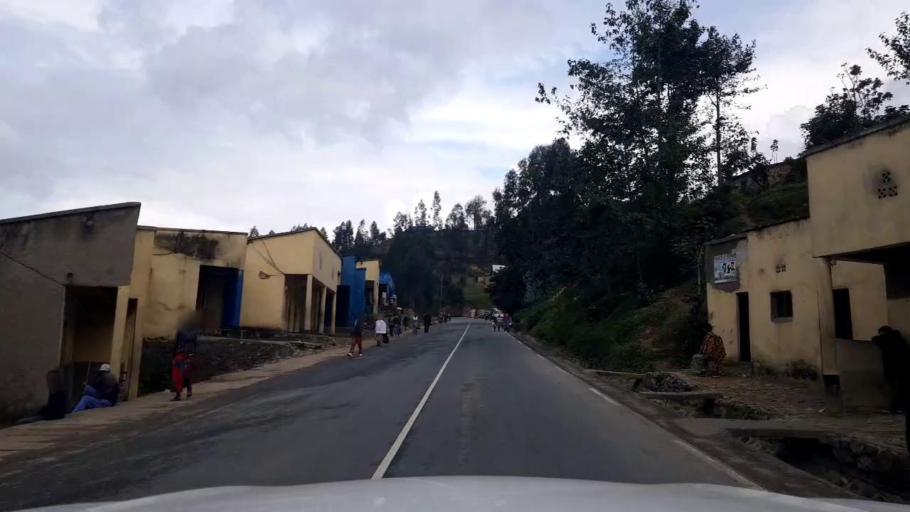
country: RW
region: Northern Province
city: Musanze
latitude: -1.6871
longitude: 29.5173
